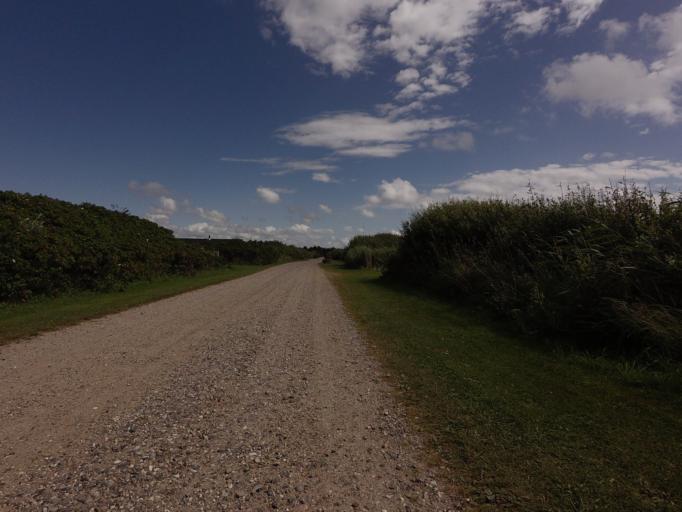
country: DK
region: North Denmark
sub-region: Jammerbugt Kommune
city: Pandrup
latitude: 57.3579
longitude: 9.6995
